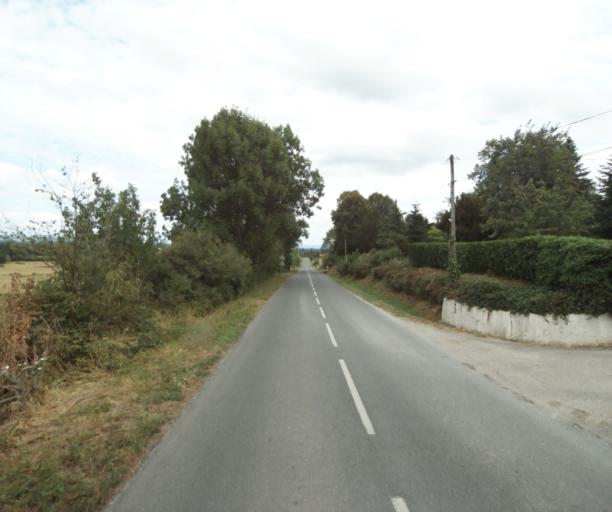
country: FR
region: Midi-Pyrenees
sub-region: Departement de la Haute-Garonne
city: Revel
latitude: 43.4440
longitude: 1.9884
